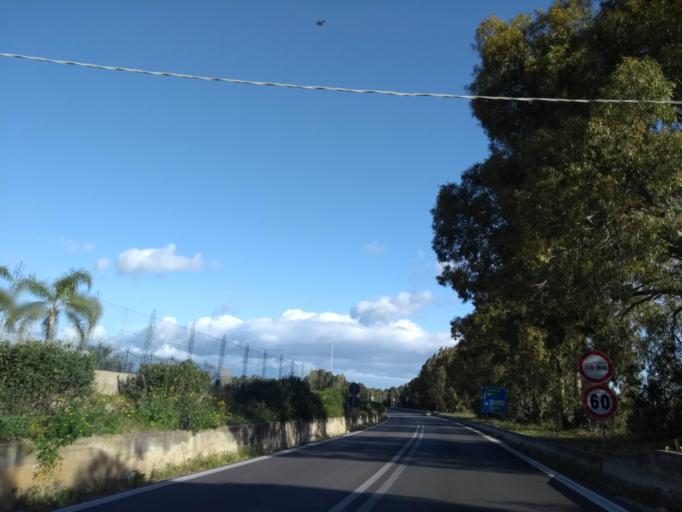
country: IT
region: Sicily
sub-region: Trapani
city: Alcamo
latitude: 38.0129
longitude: 12.9603
